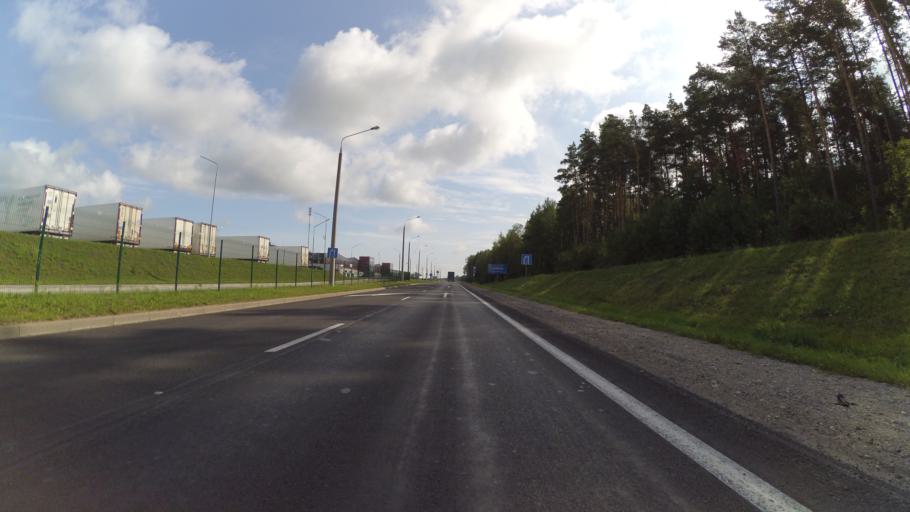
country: PL
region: Podlasie
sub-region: Powiat sokolski
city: Kuznica
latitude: 53.5257
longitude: 23.6734
